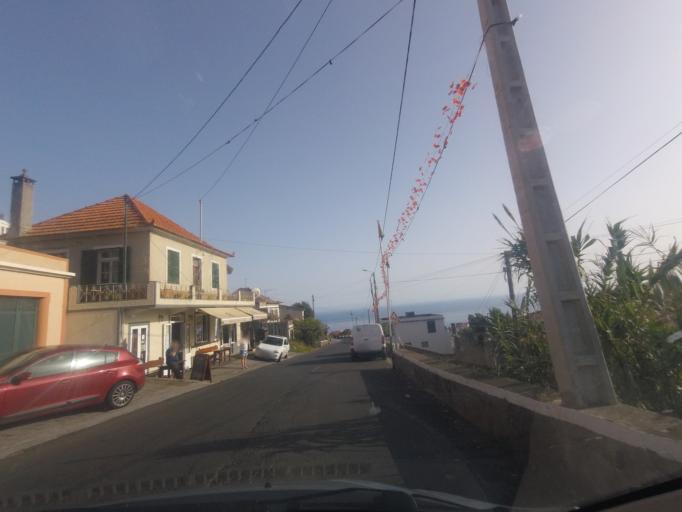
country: PT
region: Madeira
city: Ponta do Sol
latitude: 32.6953
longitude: -17.1114
